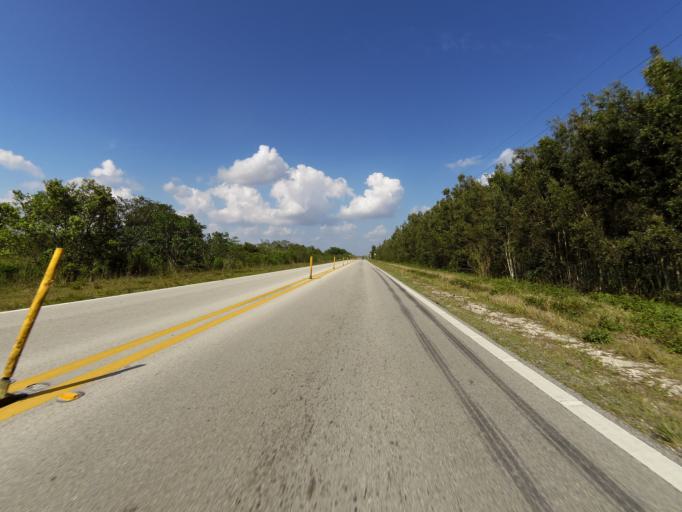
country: US
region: Florida
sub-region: Miami-Dade County
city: Palm Springs North
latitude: 25.9225
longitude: -80.4567
